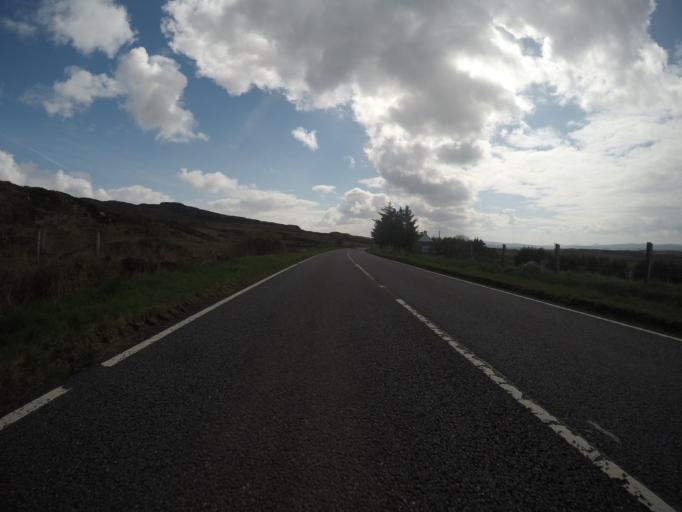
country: GB
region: Scotland
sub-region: Highland
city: Portree
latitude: 57.5605
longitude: -6.3635
